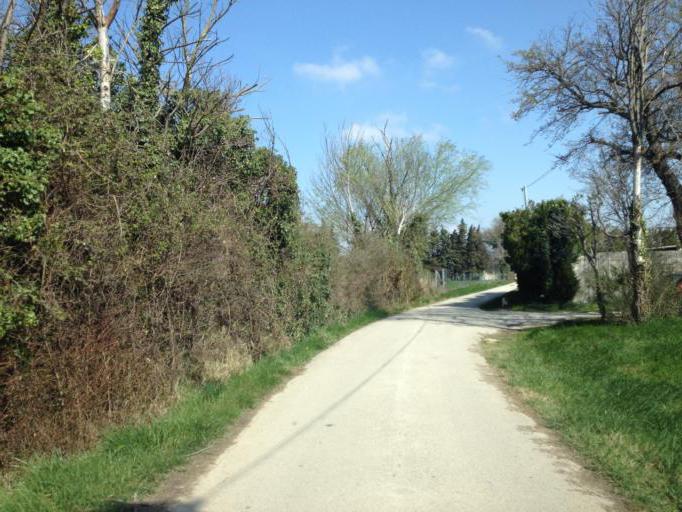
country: FR
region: Provence-Alpes-Cote d'Azur
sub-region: Departement du Vaucluse
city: Jonquieres
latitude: 44.1008
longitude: 4.9045
